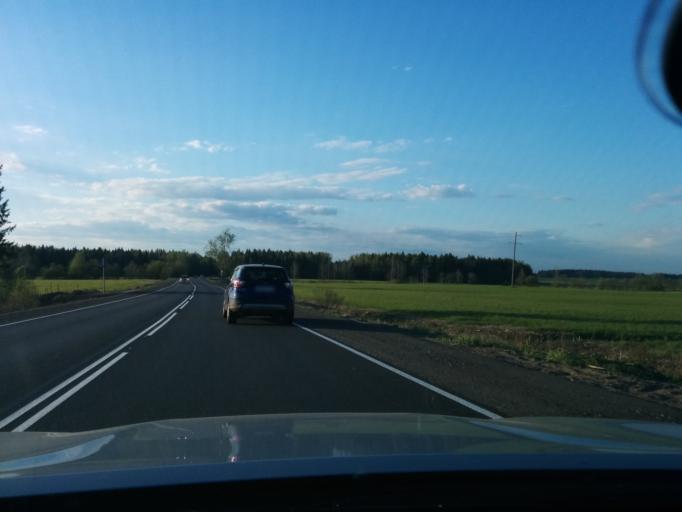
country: RU
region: Leningrad
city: Verkhniye Osel'ki
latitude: 60.2007
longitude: 30.4265
